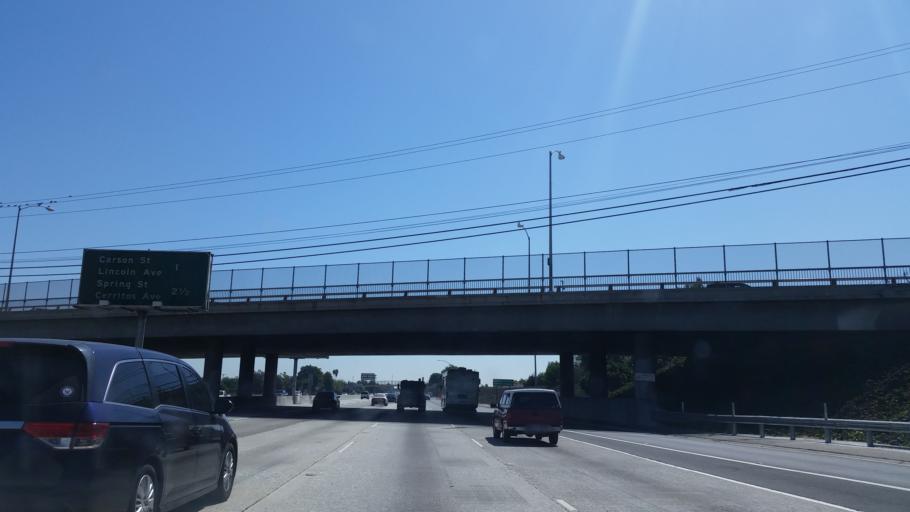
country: US
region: California
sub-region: Los Angeles County
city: Artesia
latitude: 33.8465
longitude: -118.0930
